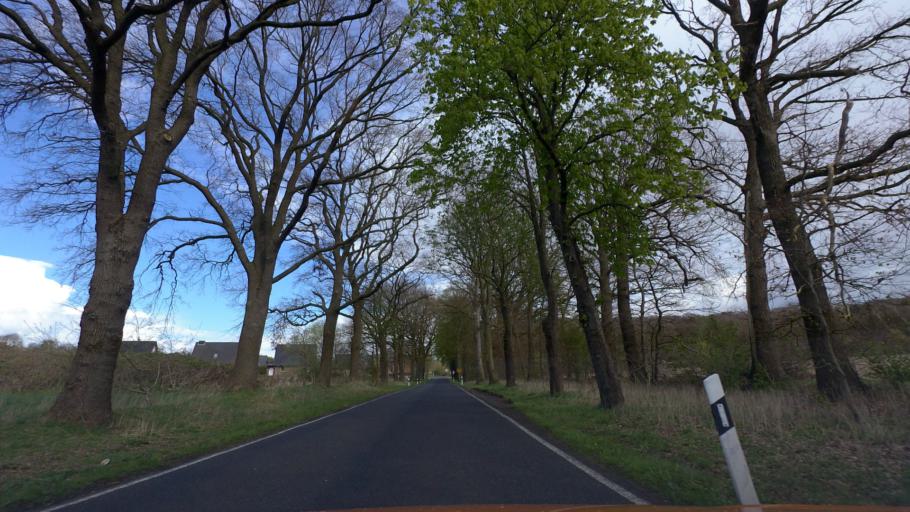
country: DE
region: Mecklenburg-Vorpommern
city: Boizenburg
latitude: 53.4292
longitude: 10.7370
